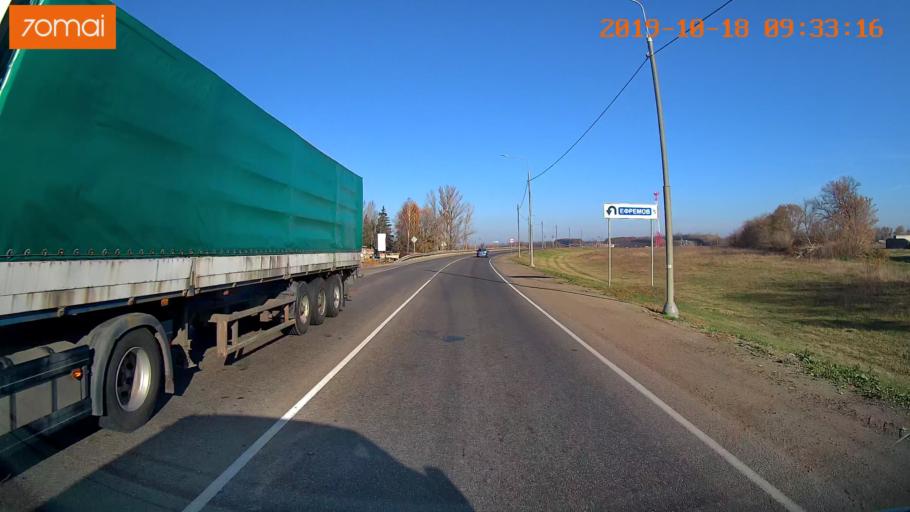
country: RU
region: Tula
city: Yefremov
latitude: 53.1649
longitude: 38.1516
